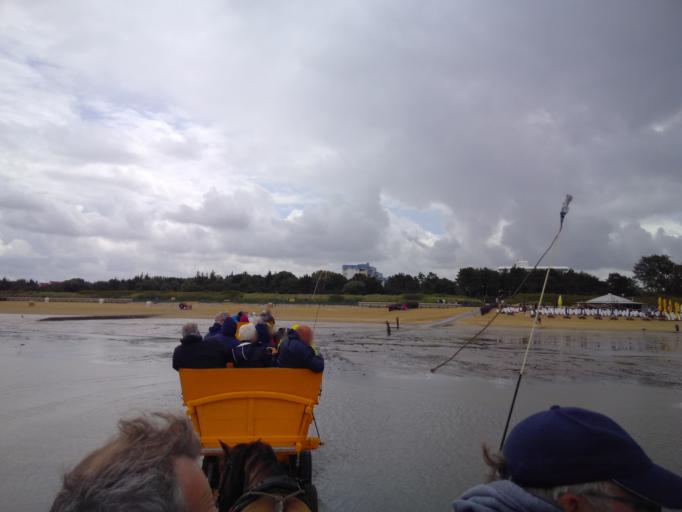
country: DE
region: Lower Saxony
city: Cuxhaven
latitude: 53.8890
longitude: 8.6468
